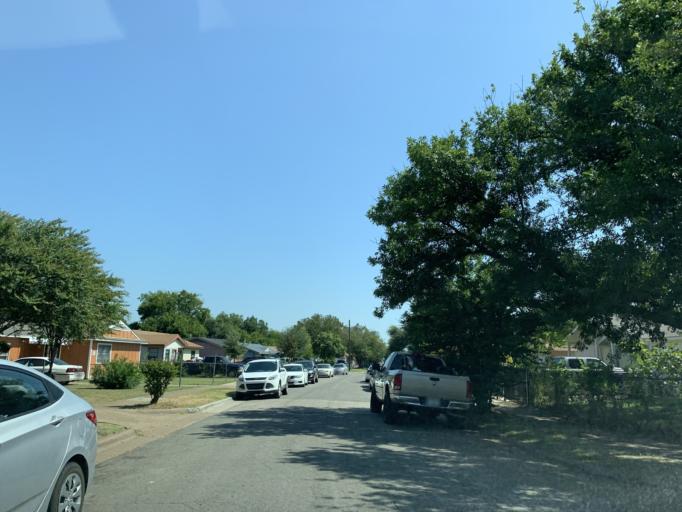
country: US
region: Texas
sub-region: Dallas County
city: Hutchins
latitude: 32.6731
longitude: -96.7582
